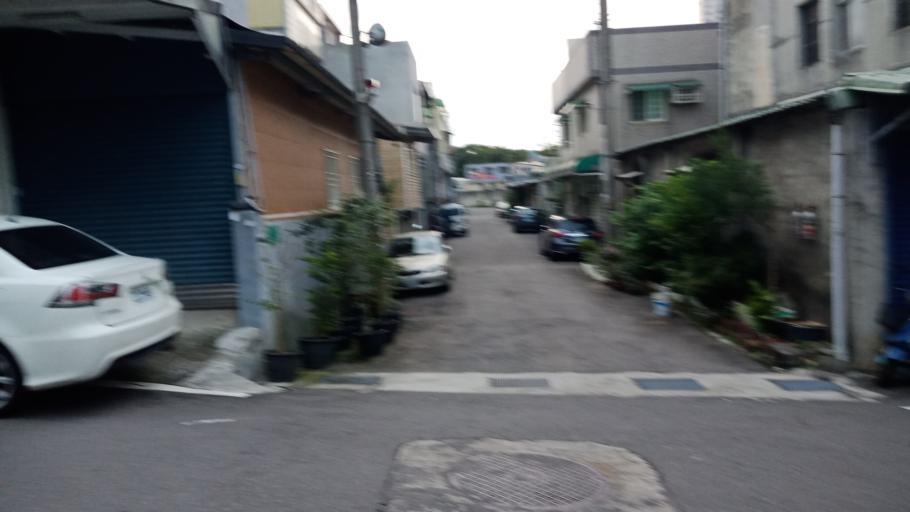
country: TW
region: Taiwan
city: Daxi
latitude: 24.8722
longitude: 121.1969
